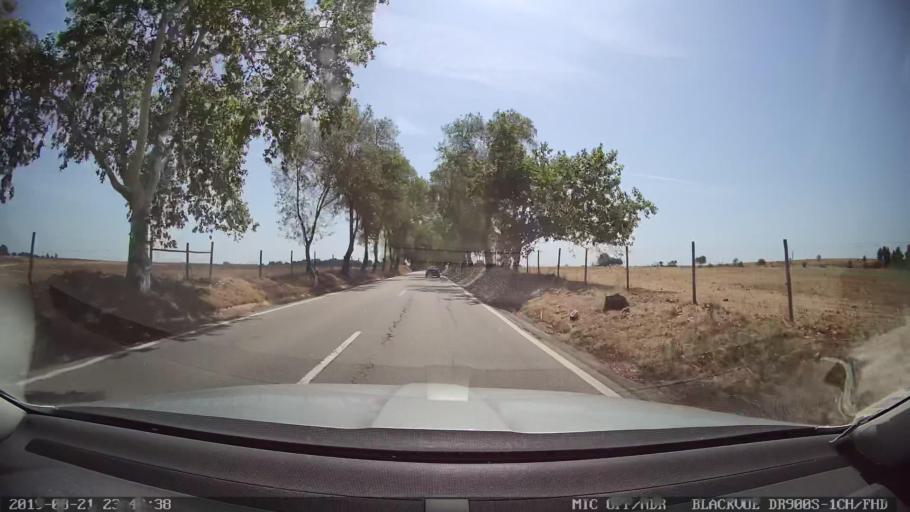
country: PT
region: Castelo Branco
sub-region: Idanha-A-Nova
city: Idanha-a-Nova
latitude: 39.8547
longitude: -7.3088
